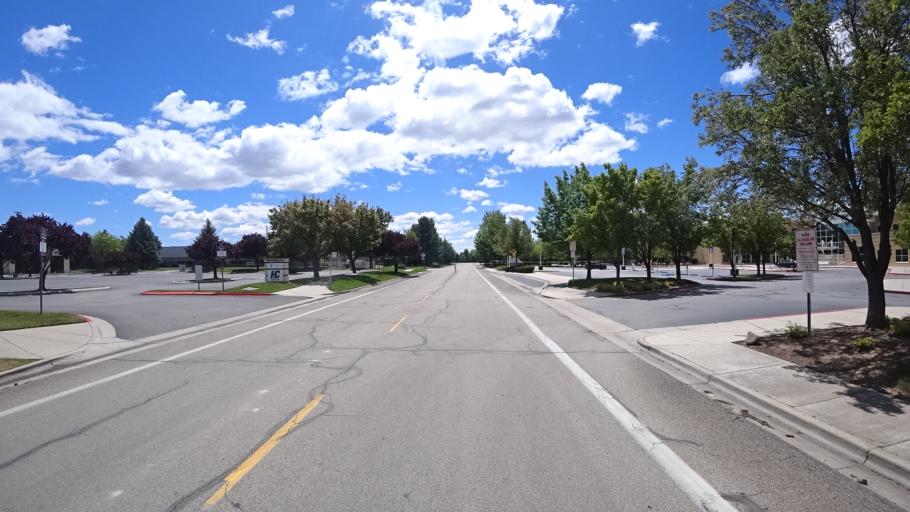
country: US
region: Idaho
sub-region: Ada County
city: Eagle
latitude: 43.6596
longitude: -116.3409
